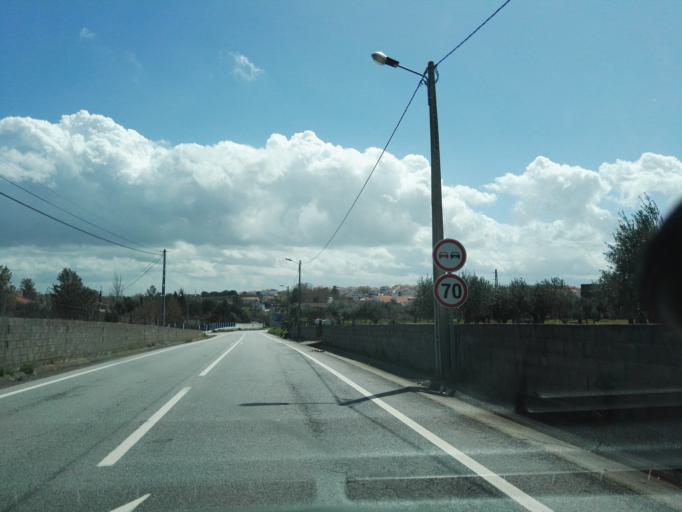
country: PT
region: Portalegre
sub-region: Arronches
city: Arronches
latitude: 39.1286
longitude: -7.2838
